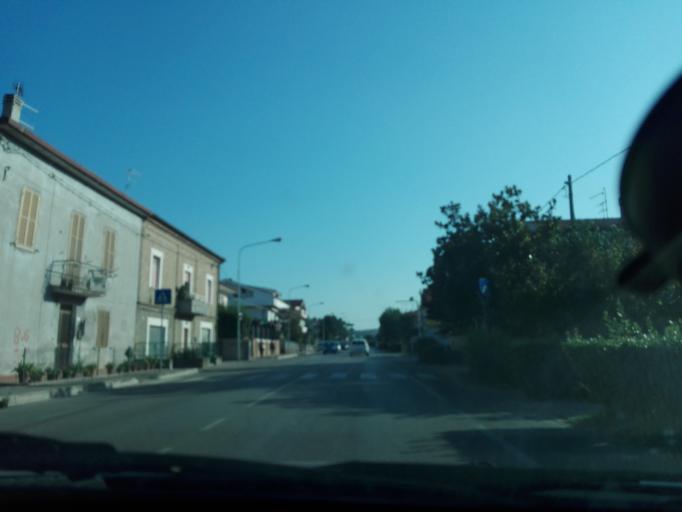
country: IT
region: Abruzzo
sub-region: Provincia di Pescara
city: Cappelle sul Tavo
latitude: 42.4902
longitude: 14.1223
